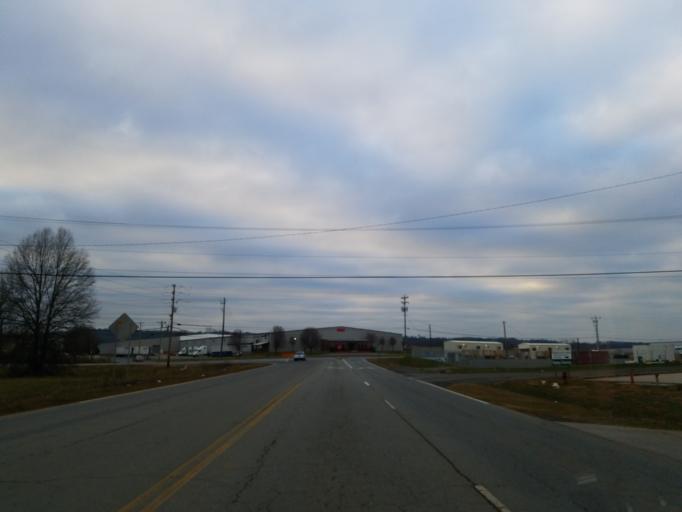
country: US
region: Georgia
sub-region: Gordon County
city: Calhoun
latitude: 34.4431
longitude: -84.9344
